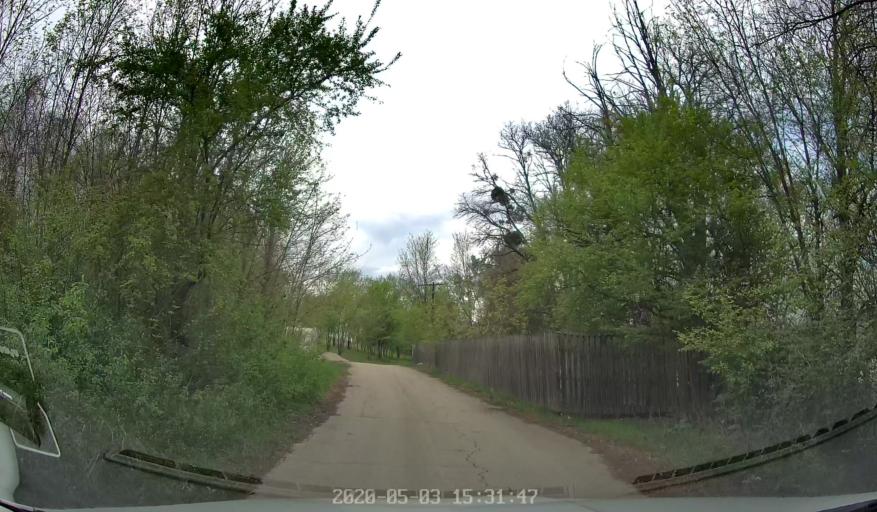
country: MD
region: Chisinau
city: Vatra
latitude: 47.0990
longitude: 28.7064
